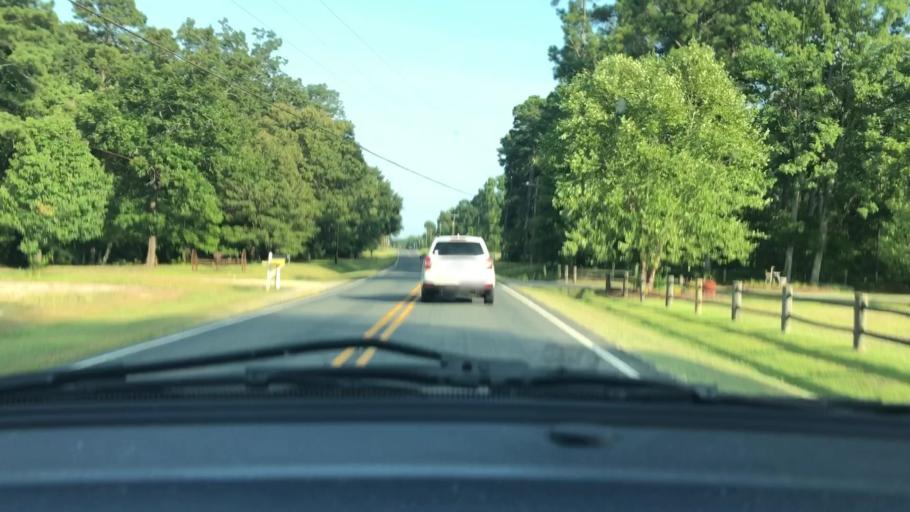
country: US
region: North Carolina
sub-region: Lee County
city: Broadway
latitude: 35.3539
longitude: -79.0764
